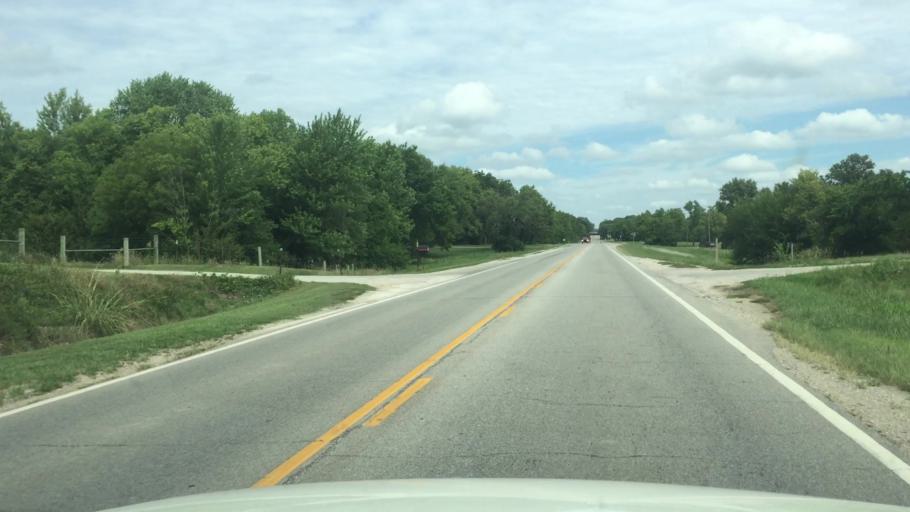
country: US
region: Kansas
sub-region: Anderson County
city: Garnett
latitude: 38.2658
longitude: -95.2490
